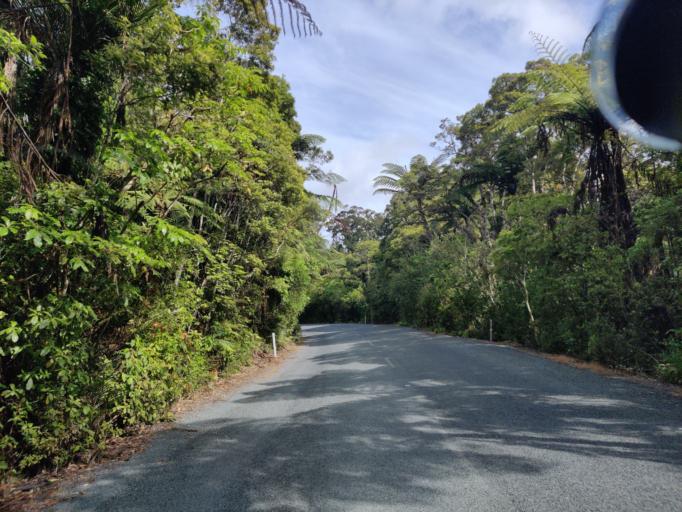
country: NZ
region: Northland
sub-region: Far North District
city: Waimate North
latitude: -35.6019
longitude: 173.5291
